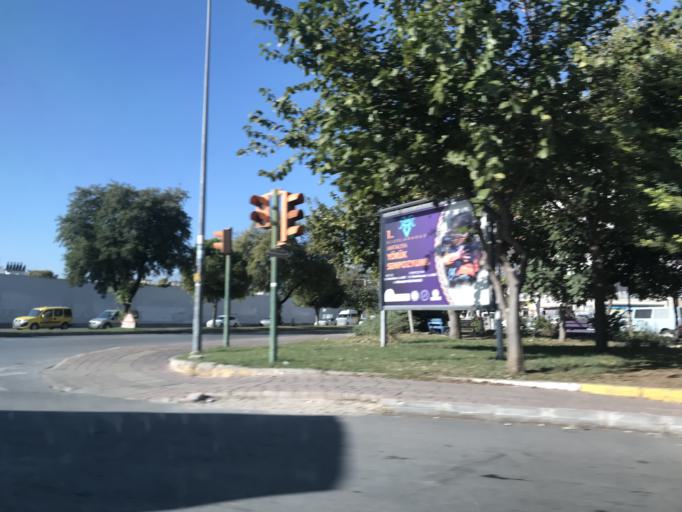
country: TR
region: Antalya
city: Antalya
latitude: 36.9000
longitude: 30.7059
